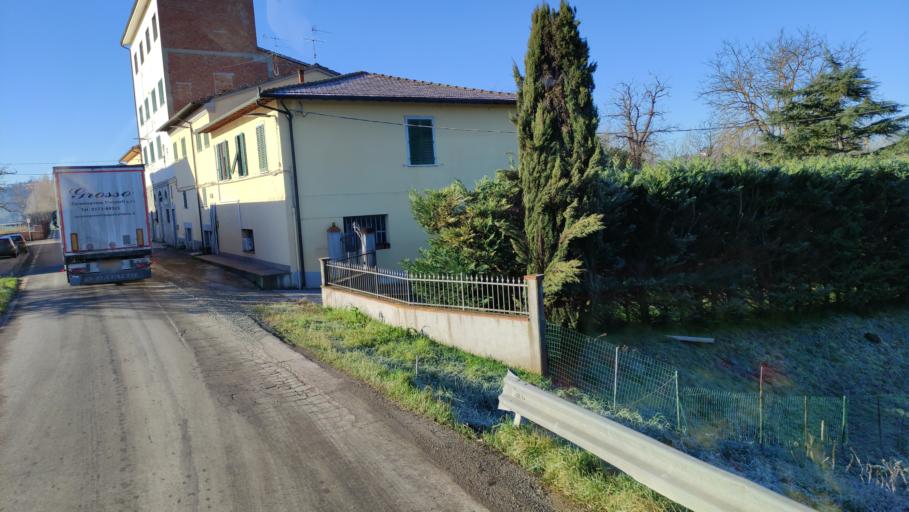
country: IT
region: Tuscany
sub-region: Province of Florence
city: Castelfiorentino
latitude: 43.6489
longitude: 10.9480
